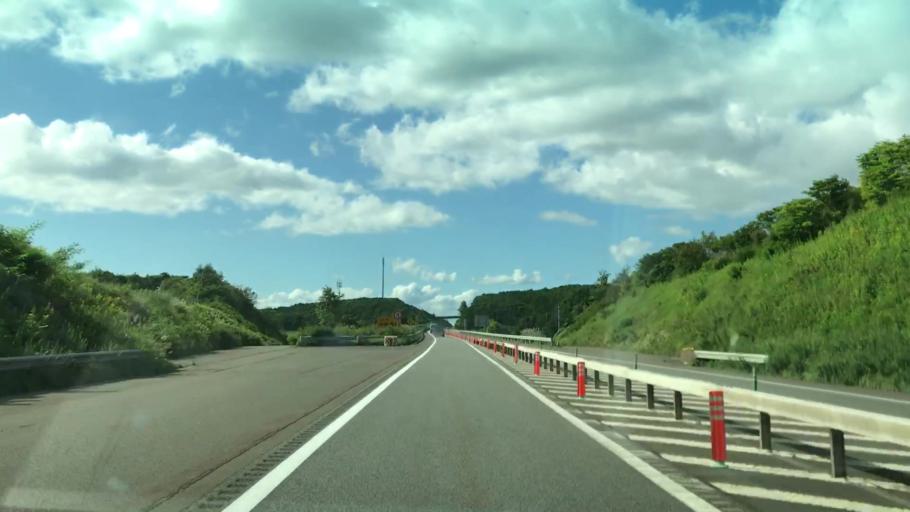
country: JP
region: Hokkaido
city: Muroran
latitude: 42.3914
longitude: 140.9598
